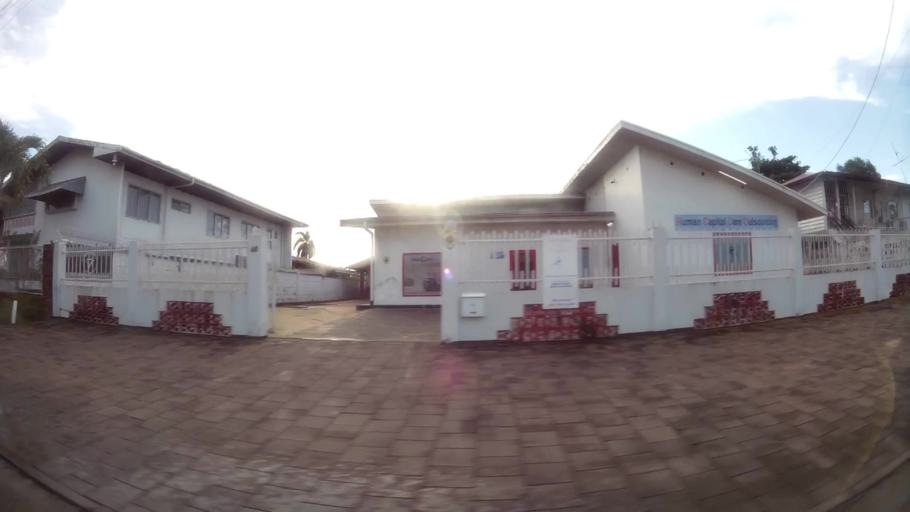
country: SR
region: Paramaribo
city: Paramaribo
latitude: 5.8288
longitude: -55.1828
